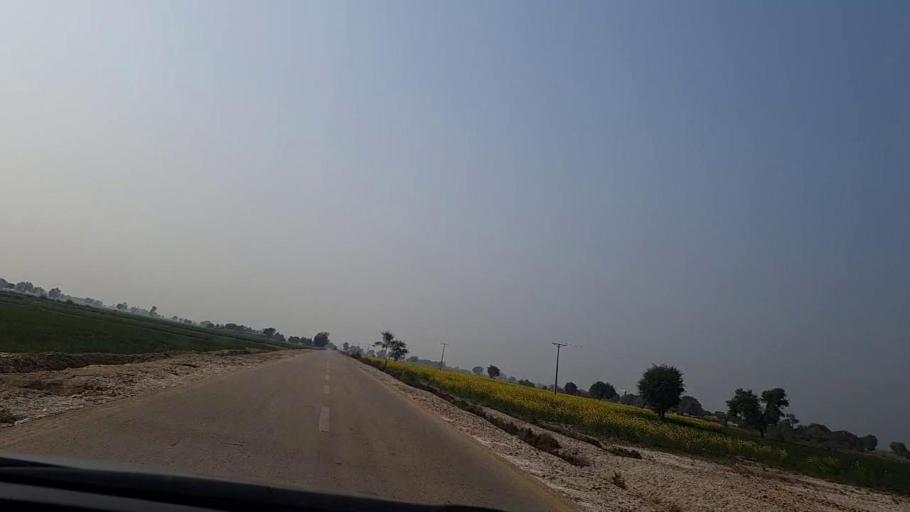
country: PK
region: Sindh
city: Sakrand
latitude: 26.1343
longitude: 68.1979
